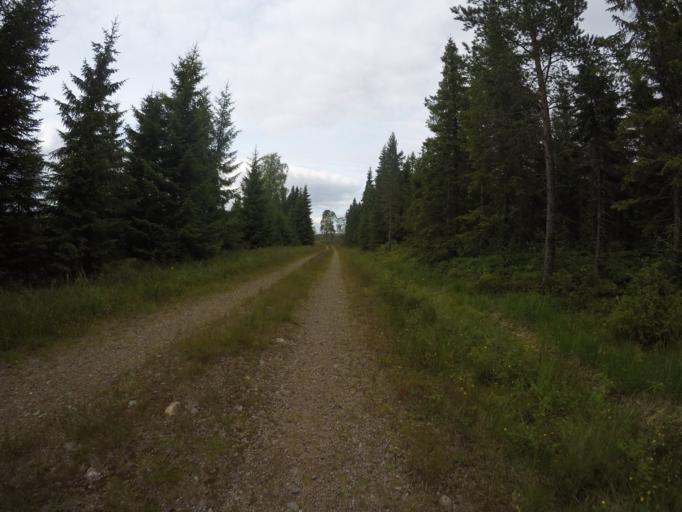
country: SE
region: Vaermland
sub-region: Filipstads Kommun
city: Lesjofors
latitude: 60.2009
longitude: 14.2594
